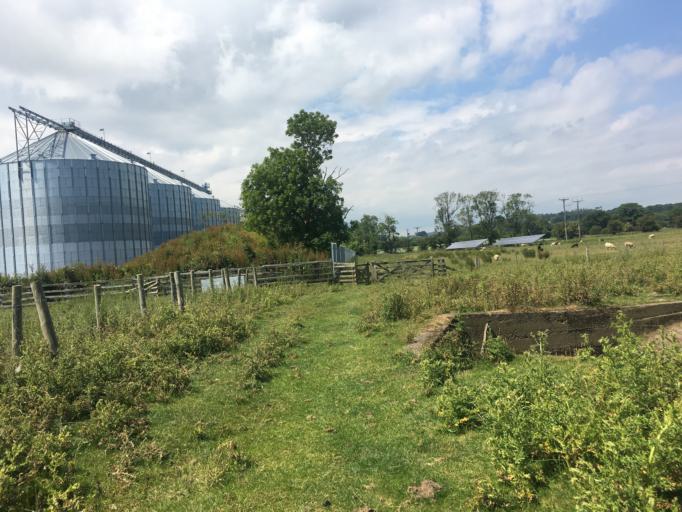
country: GB
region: England
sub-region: Northumberland
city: Belford
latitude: 55.5980
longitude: -1.8075
